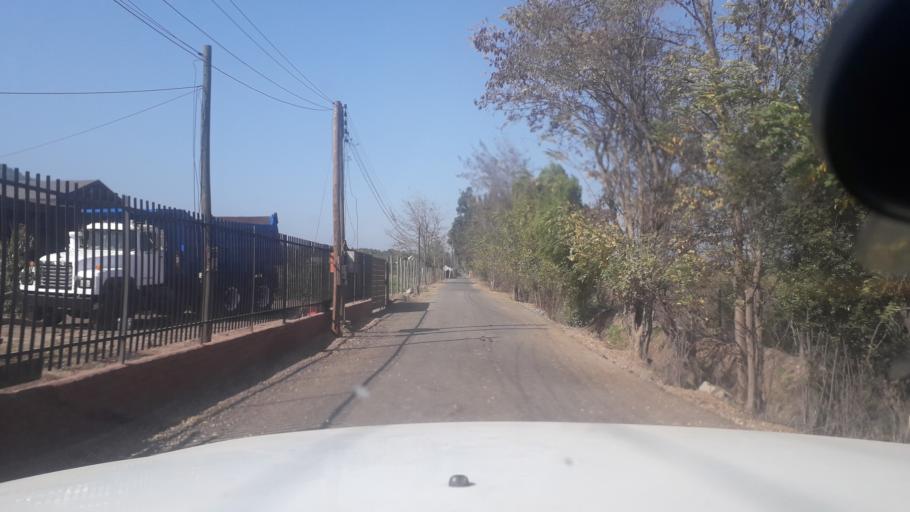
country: CL
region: Valparaiso
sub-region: Provincia de San Felipe
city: Llaillay
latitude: -32.8215
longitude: -71.0243
